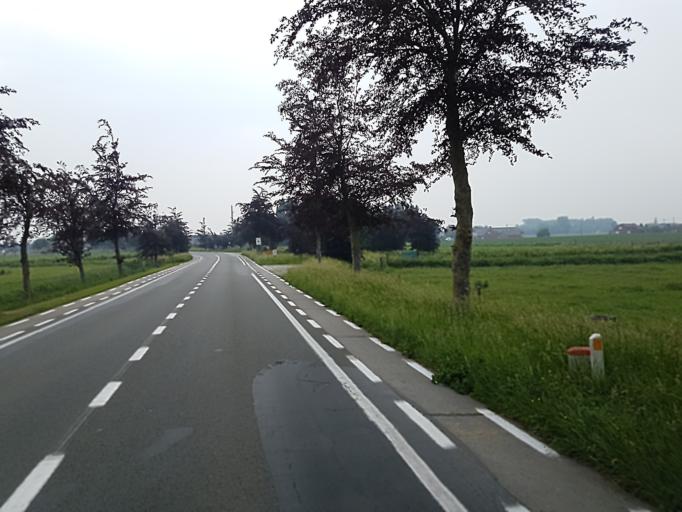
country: BE
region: Flanders
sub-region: Provincie West-Vlaanderen
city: Tielt
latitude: 50.9643
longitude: 3.3616
